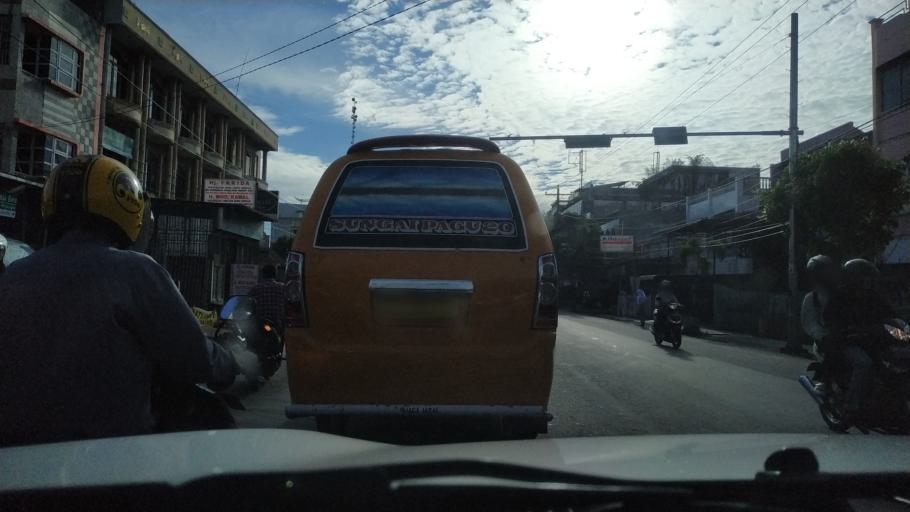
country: ID
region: North Sumatra
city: Medan
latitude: 3.5982
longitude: 98.7012
